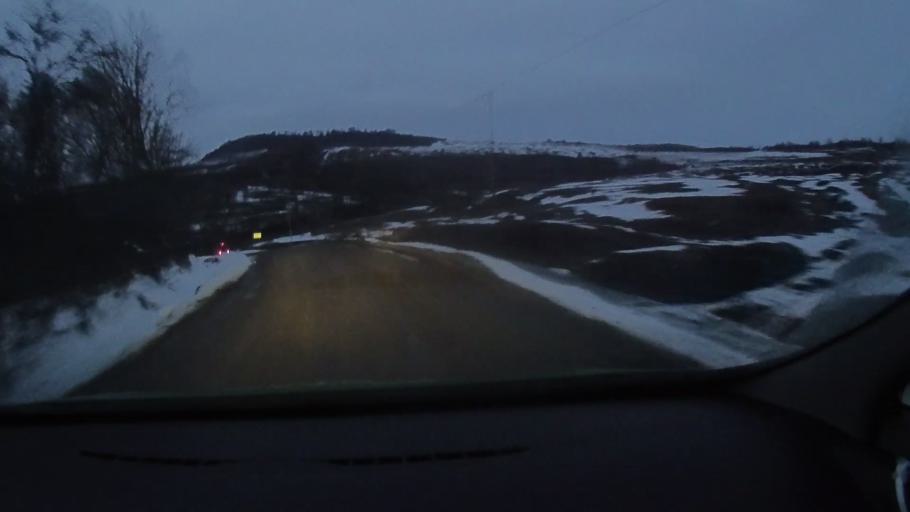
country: RO
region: Harghita
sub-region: Comuna Darjiu
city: Darjiu
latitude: 46.1762
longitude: 25.2426
